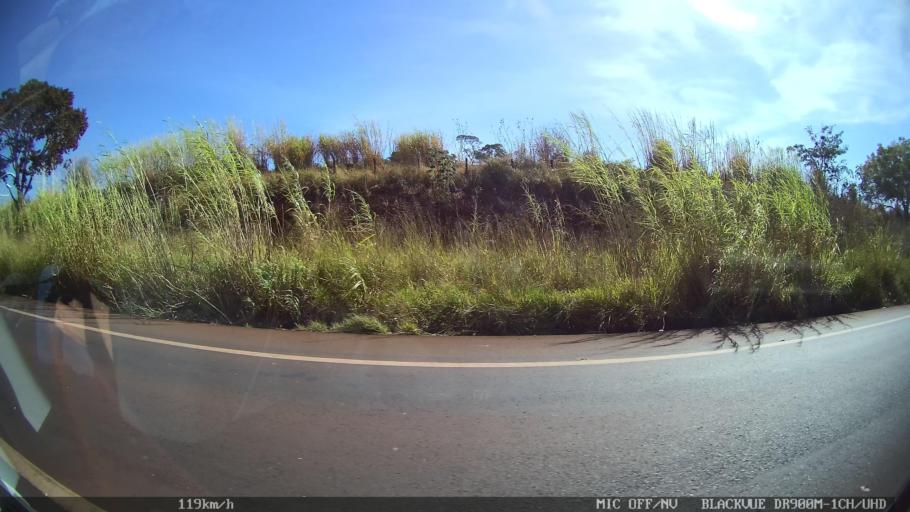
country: BR
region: Sao Paulo
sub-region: Sao Joaquim Da Barra
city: Sao Joaquim da Barra
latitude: -20.5585
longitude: -47.6824
